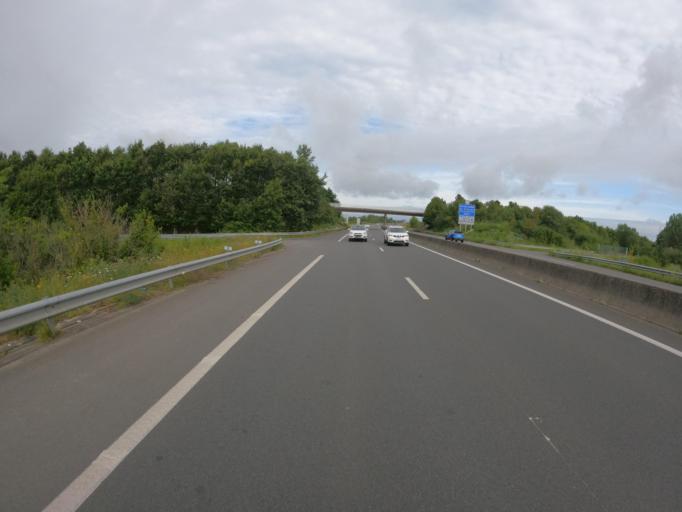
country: FR
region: Centre
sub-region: Departement d'Indre-et-Loire
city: Villandry
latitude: 47.3063
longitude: 0.5174
